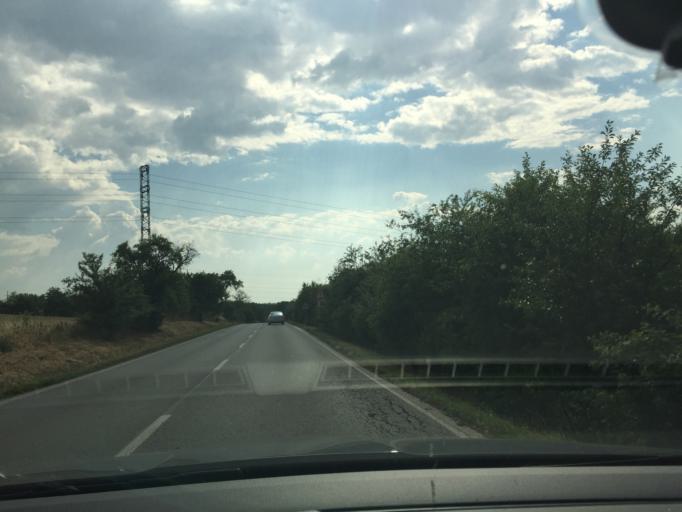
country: CZ
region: Central Bohemia
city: Kralupy nad Vltavou
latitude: 50.2395
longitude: 14.3441
